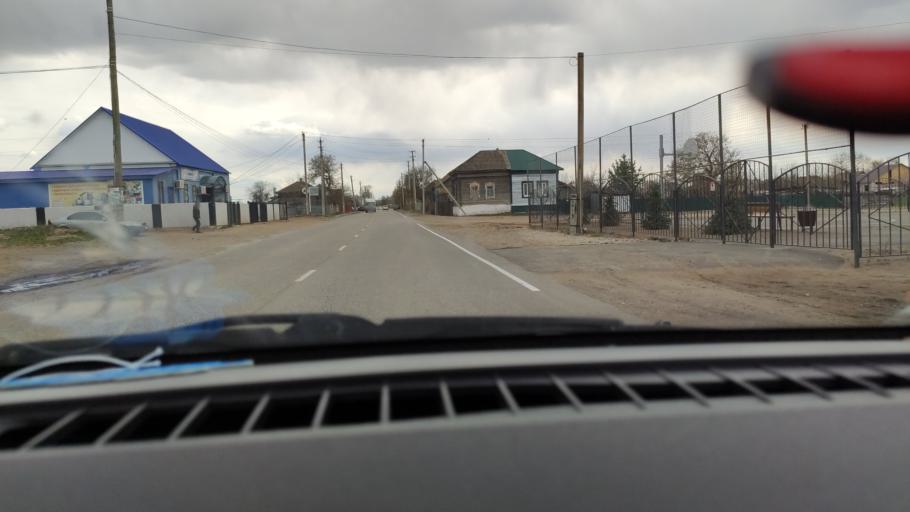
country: RU
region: Saratov
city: Privolzhskiy
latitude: 51.2005
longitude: 45.9163
